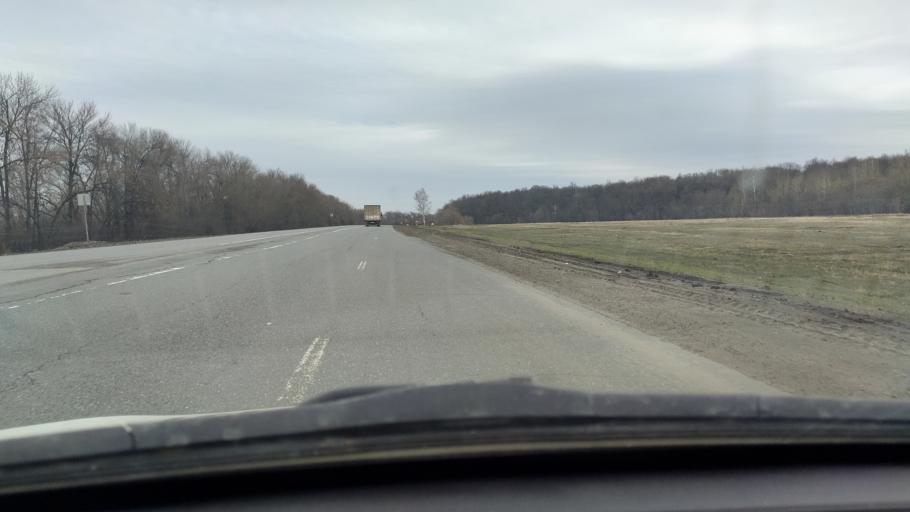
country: RU
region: Samara
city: Zhigulevsk
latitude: 53.2852
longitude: 49.3245
